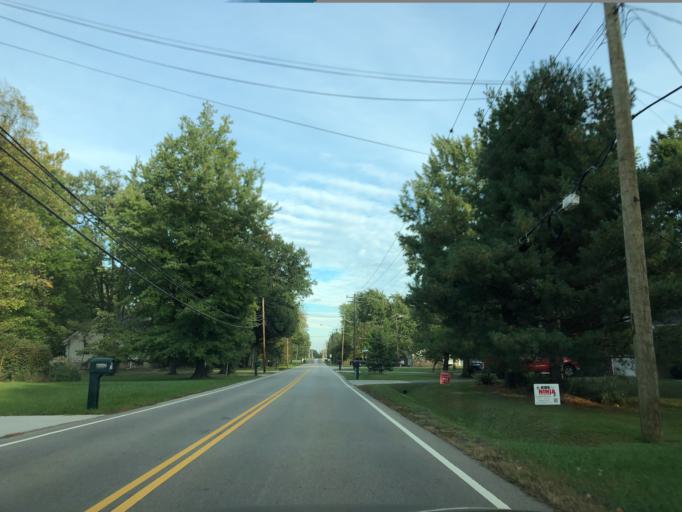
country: US
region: Ohio
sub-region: Warren County
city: Landen
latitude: 39.2820
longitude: -84.2933
